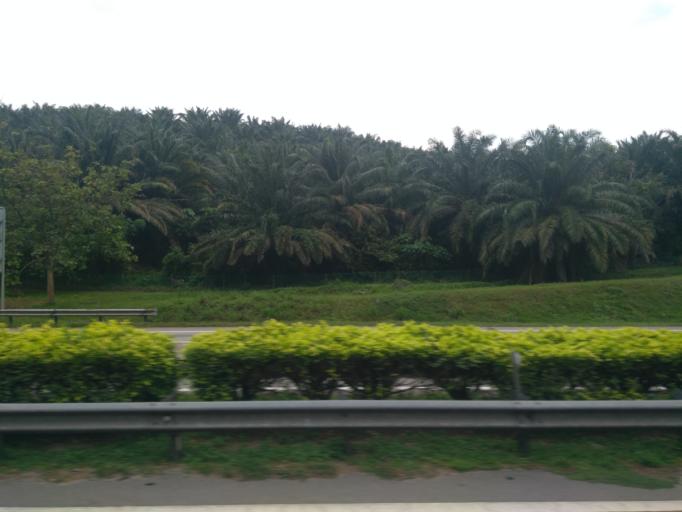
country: MY
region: Negeri Sembilan
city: Tampin
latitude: 2.4519
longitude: 102.1692
